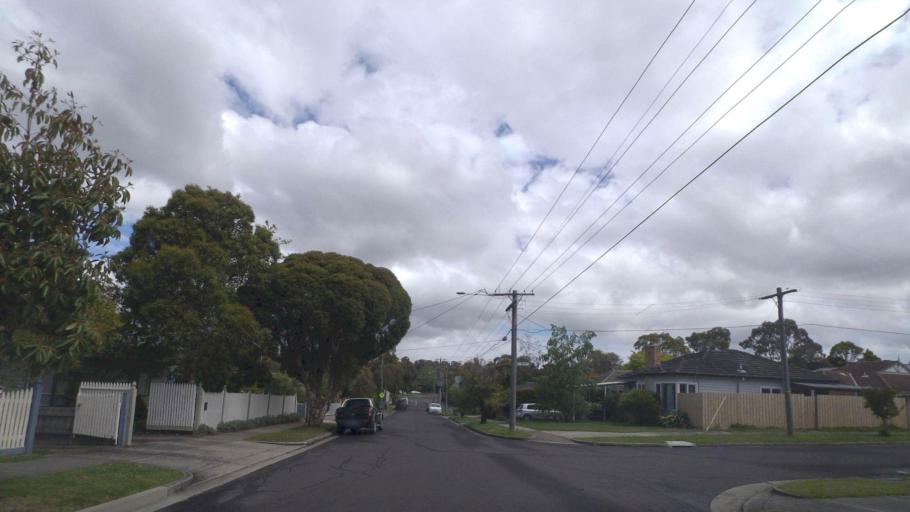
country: AU
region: Victoria
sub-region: Whitehorse
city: Vermont
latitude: -37.8321
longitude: 145.2077
